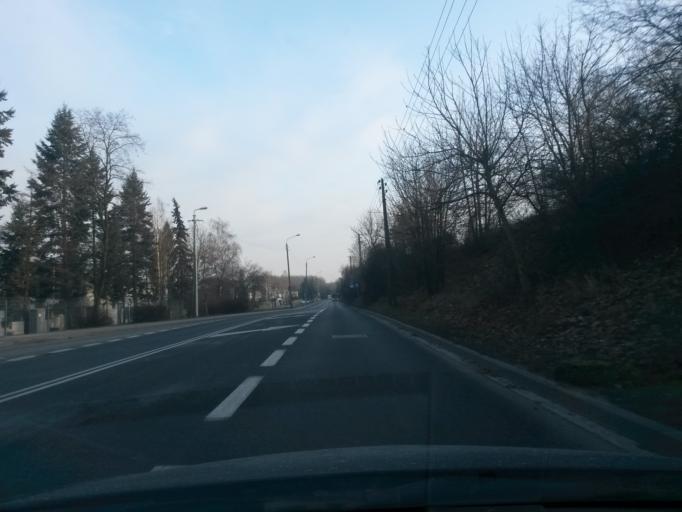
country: PL
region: Greater Poland Voivodeship
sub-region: Powiat poznanski
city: Czerwonak
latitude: 52.4242
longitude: 16.9904
